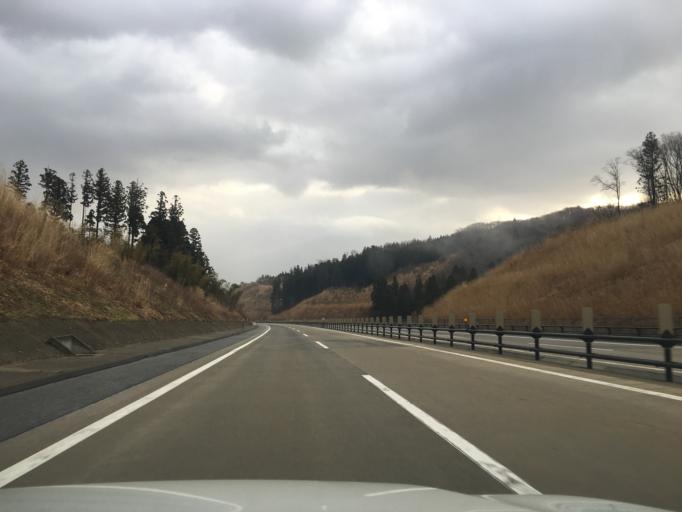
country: JP
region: Yamagata
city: Tsuruoka
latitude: 38.6981
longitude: 139.7119
